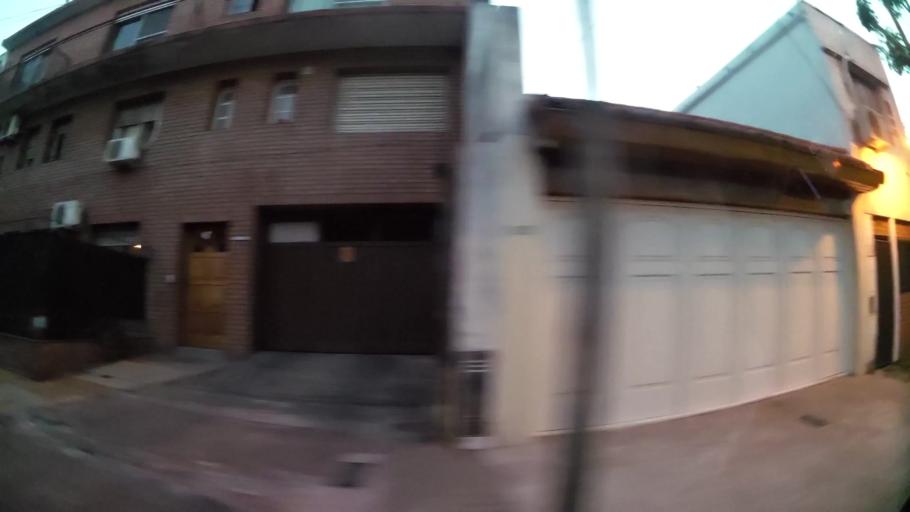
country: AR
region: Buenos Aires
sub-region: Partido de Tigre
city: Tigre
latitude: -34.4401
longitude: -58.5550
